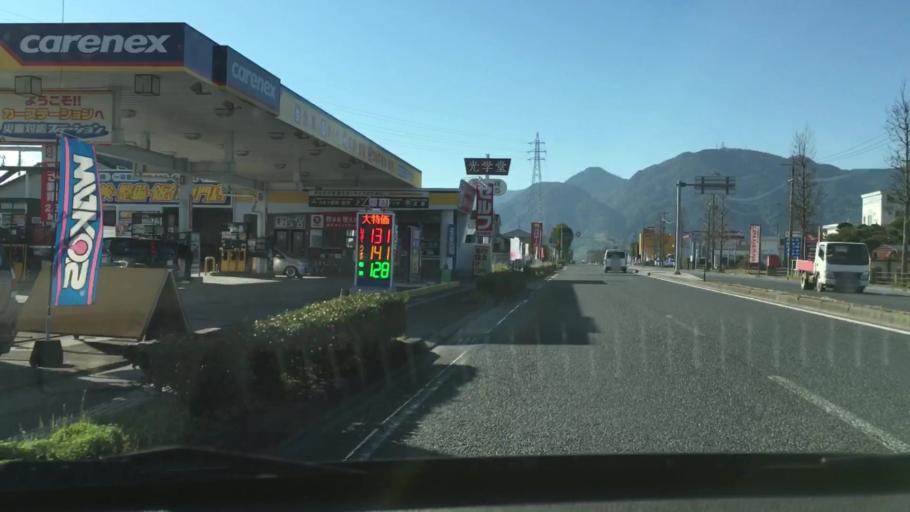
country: JP
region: Kagoshima
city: Kajiki
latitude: 31.7257
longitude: 130.6239
